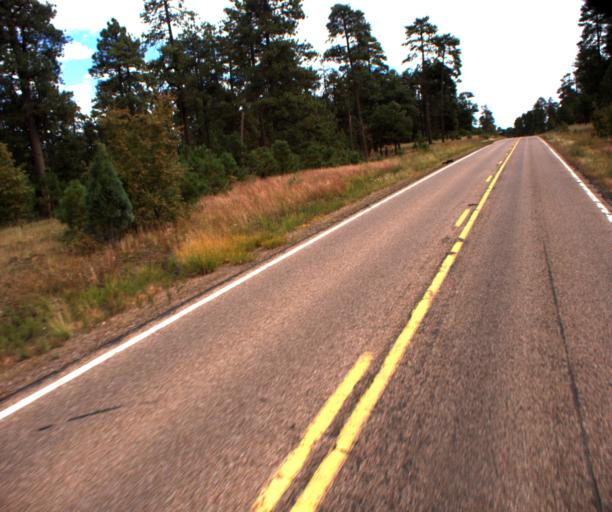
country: US
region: Arizona
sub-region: Navajo County
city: Heber-Overgaard
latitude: 34.3373
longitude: -110.7354
